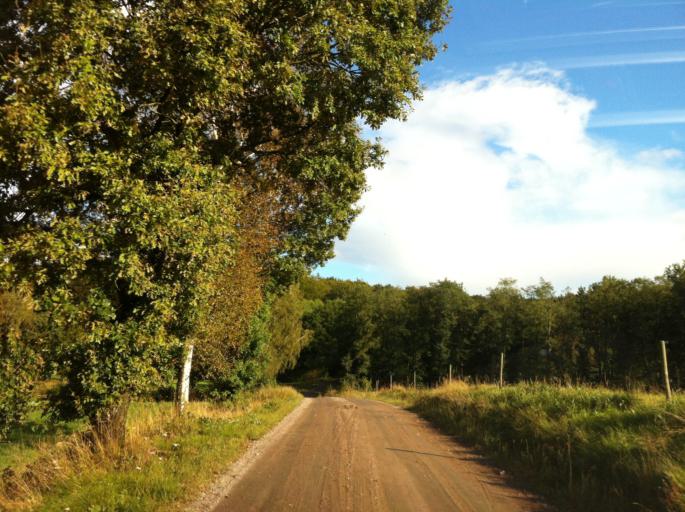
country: SE
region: Skane
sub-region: Perstorps Kommun
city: Perstorp
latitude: 56.1376
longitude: 13.5340
